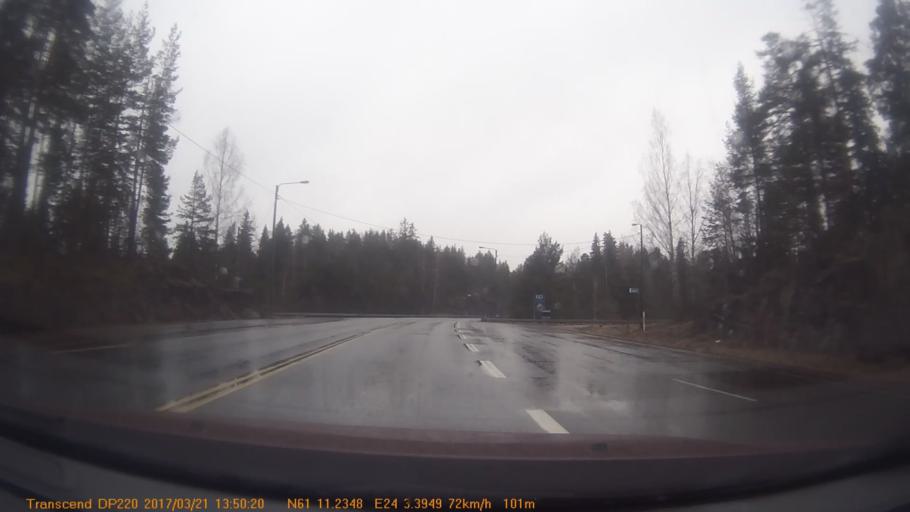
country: FI
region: Pirkanmaa
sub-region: Etelae-Pirkanmaa
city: Valkeakoski
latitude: 61.1876
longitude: 24.0569
